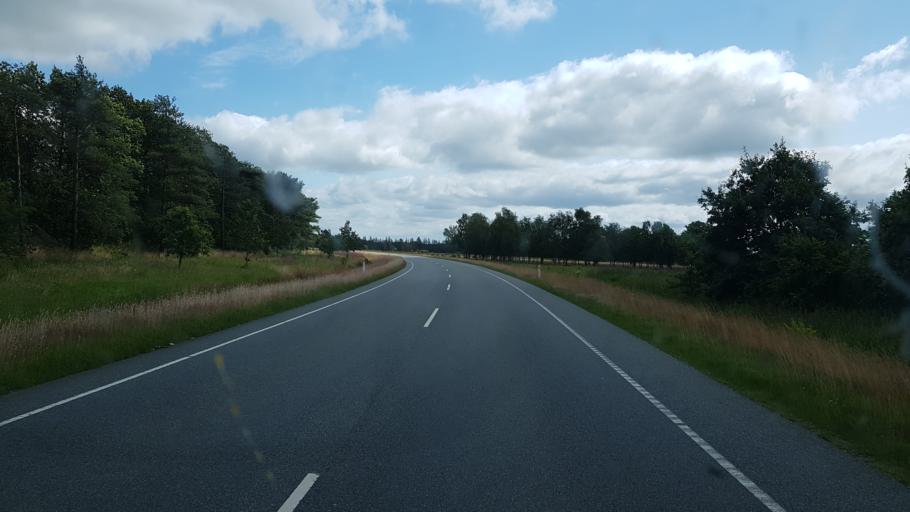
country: DK
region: South Denmark
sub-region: Billund Kommune
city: Grindsted
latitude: 55.7500
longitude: 8.9027
